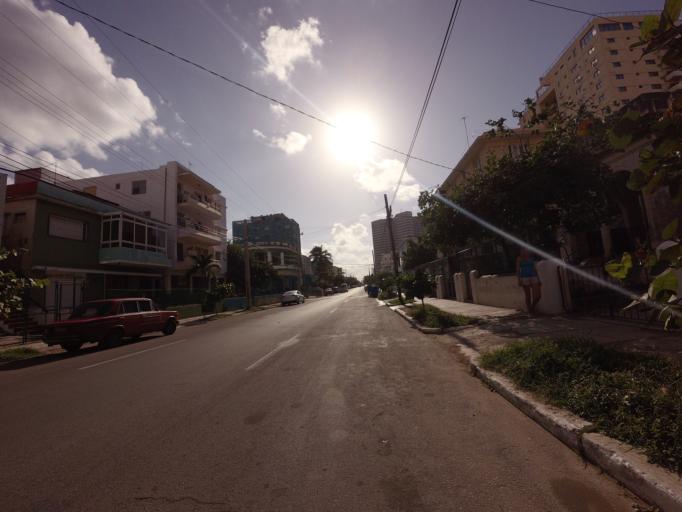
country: CU
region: La Habana
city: Havana
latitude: 23.1413
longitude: -82.3997
